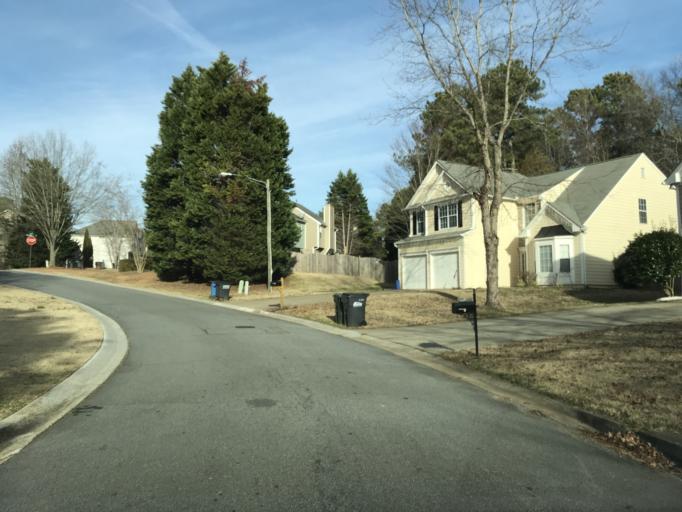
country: US
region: Georgia
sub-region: Cobb County
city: Kennesaw
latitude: 34.0588
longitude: -84.5957
